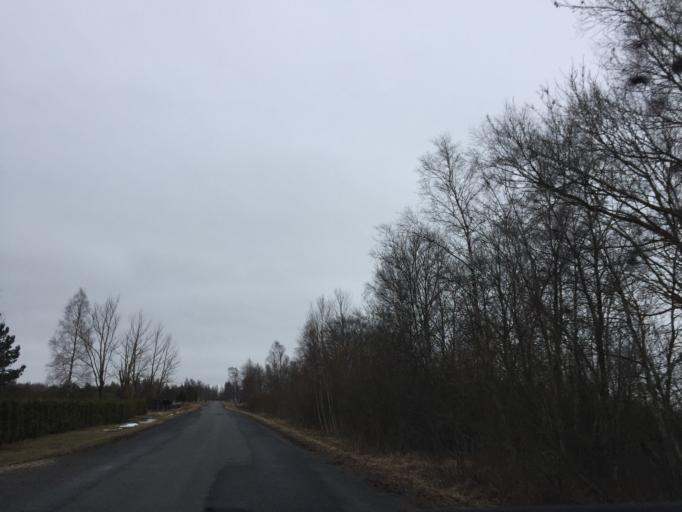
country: EE
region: Laeaene
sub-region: Haapsalu linn
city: Haapsalu
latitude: 58.7801
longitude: 23.4658
